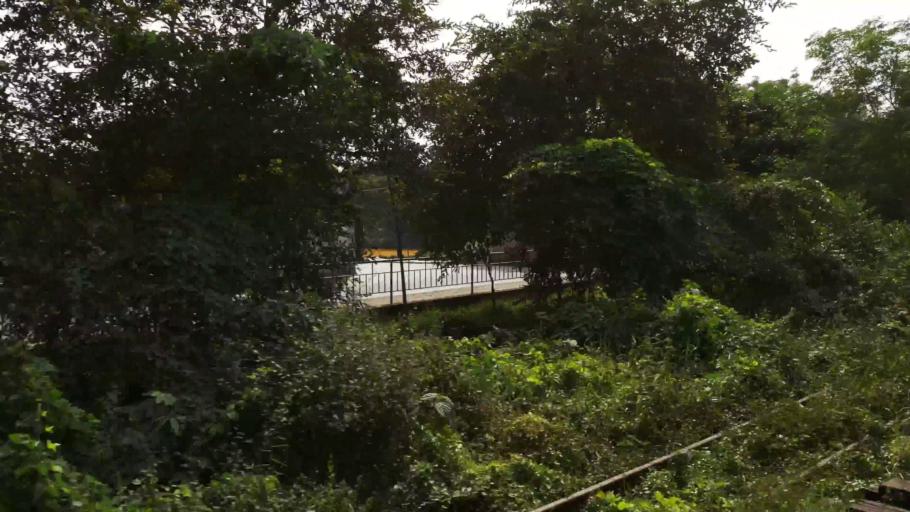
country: BD
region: Dhaka
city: Tungi
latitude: 23.8491
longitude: 90.4108
